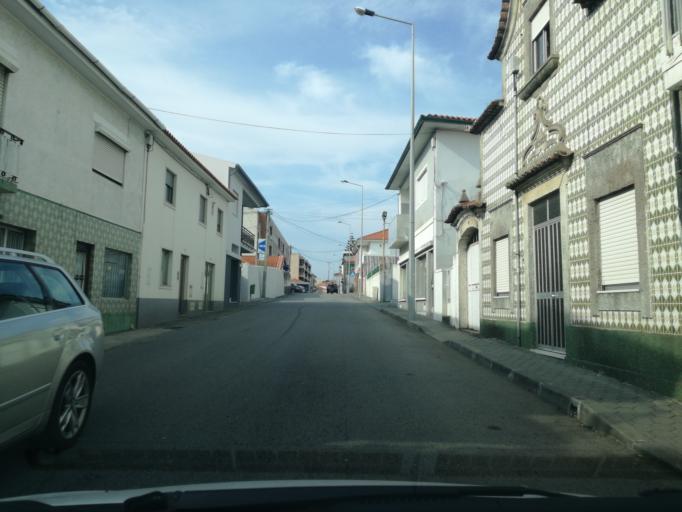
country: PT
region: Porto
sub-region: Vila Nova de Gaia
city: Sao Felix da Marinha
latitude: 41.0459
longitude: -8.6287
